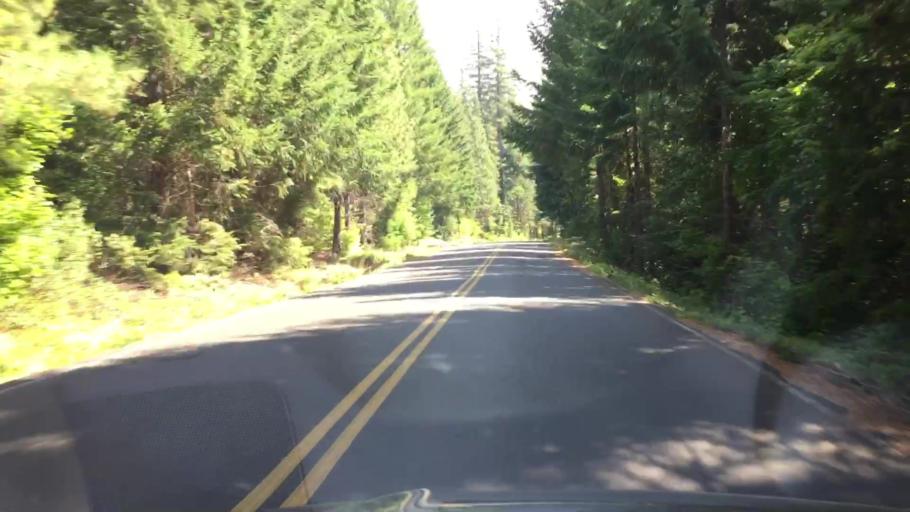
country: US
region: Washington
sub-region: Klickitat County
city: White Salmon
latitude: 46.0709
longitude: -121.5775
